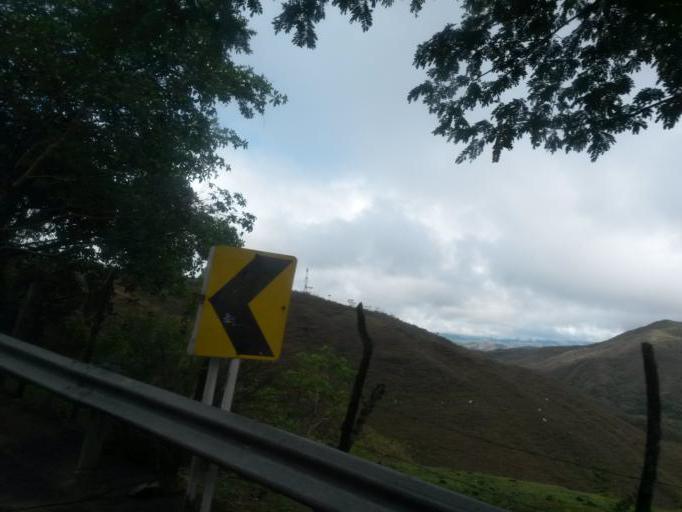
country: CO
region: Cauca
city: El Bordo
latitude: 2.1739
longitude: -76.8964
